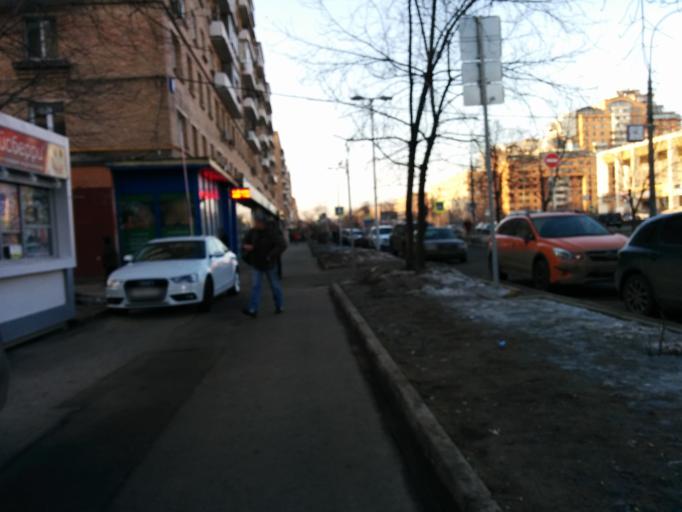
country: RU
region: Moscow
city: Novyye Cheremushki
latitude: 55.7272
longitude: 37.5828
